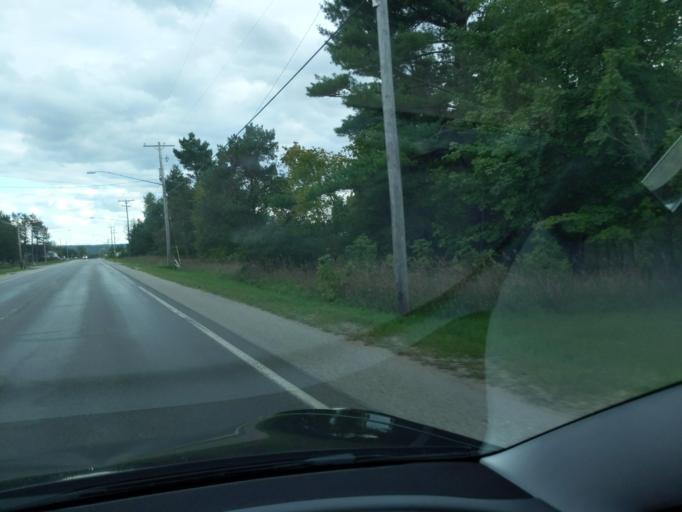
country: US
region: Michigan
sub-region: Kalkaska County
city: Rapid City
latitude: 44.8257
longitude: -85.2828
